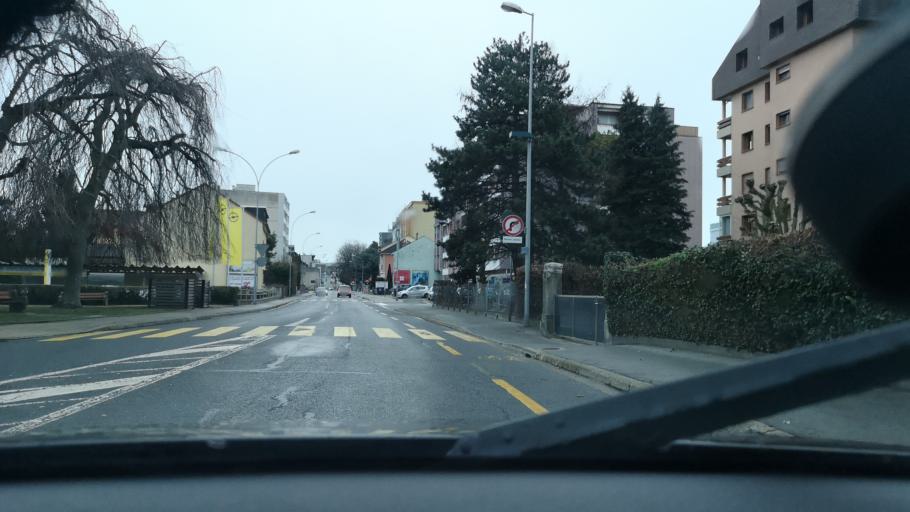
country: CH
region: Vaud
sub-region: Jura-Nord vaudois District
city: Yverdon-les-Bains
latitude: 46.7846
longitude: 6.6331
